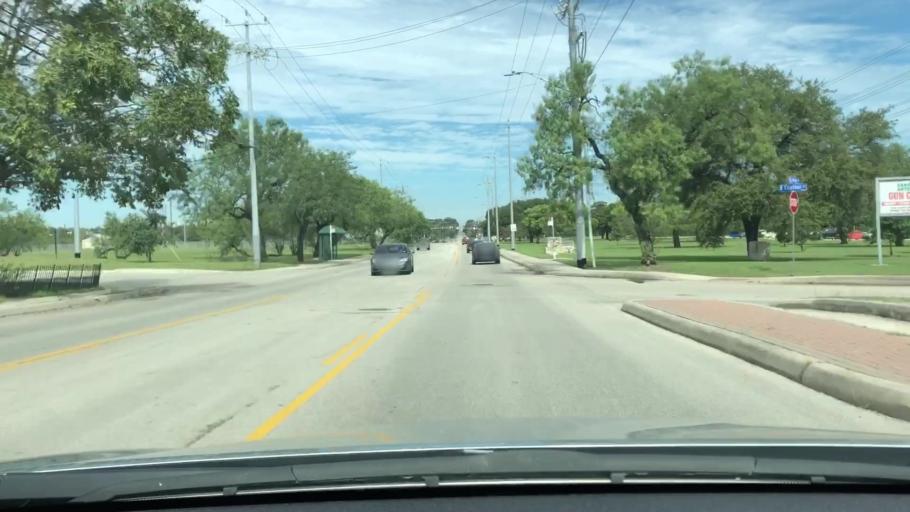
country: US
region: Texas
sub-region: Bexar County
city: Olmos Park
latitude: 29.4850
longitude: -98.4917
